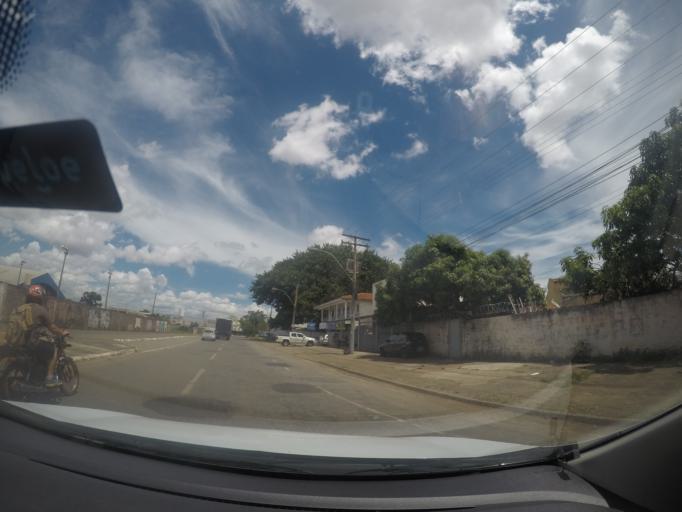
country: BR
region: Goias
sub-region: Goiania
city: Goiania
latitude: -16.6779
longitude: -49.3122
